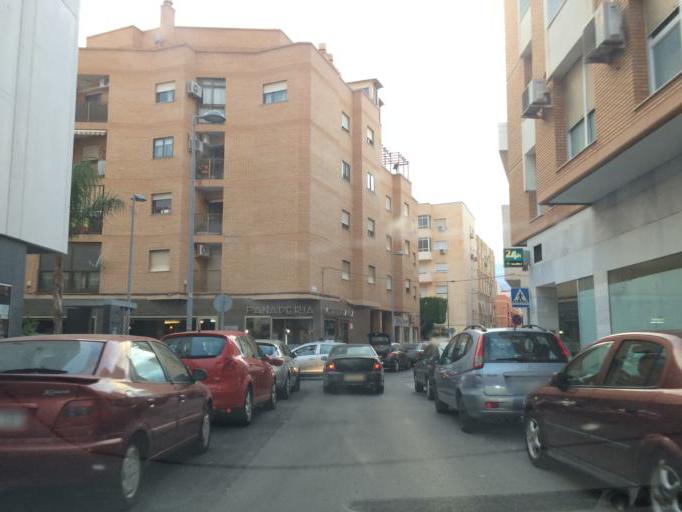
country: ES
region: Andalusia
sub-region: Provincia de Almeria
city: Almeria
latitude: 36.8343
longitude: -2.4510
